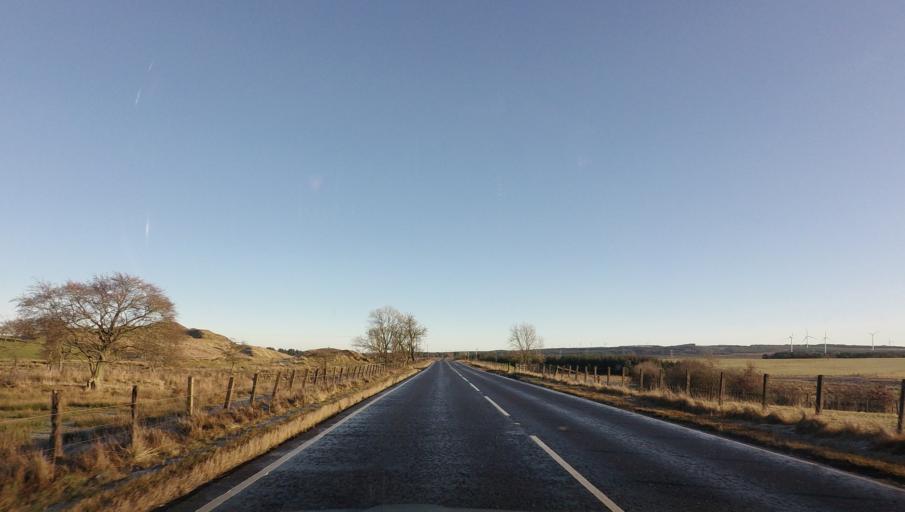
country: GB
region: Scotland
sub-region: North Lanarkshire
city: Shotts
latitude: 55.8061
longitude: -3.7586
